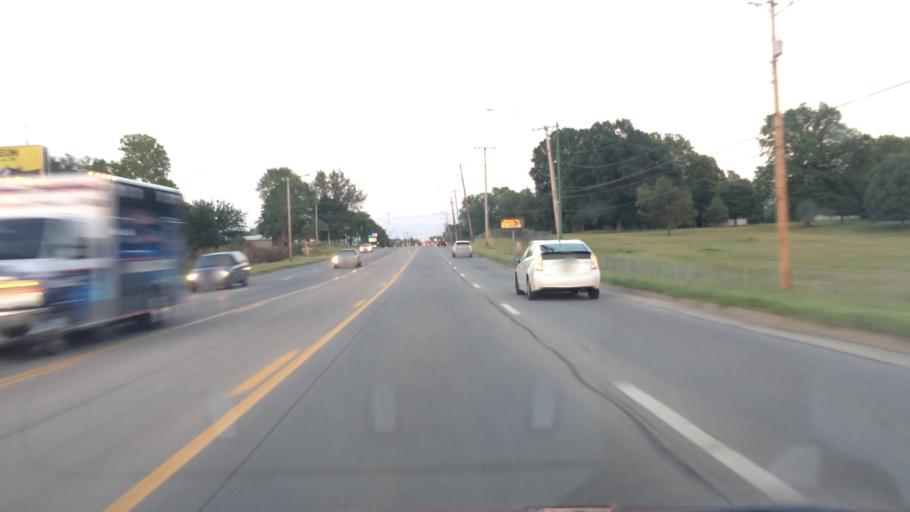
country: US
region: Missouri
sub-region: Greene County
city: Springfield
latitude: 37.1826
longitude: -93.3258
